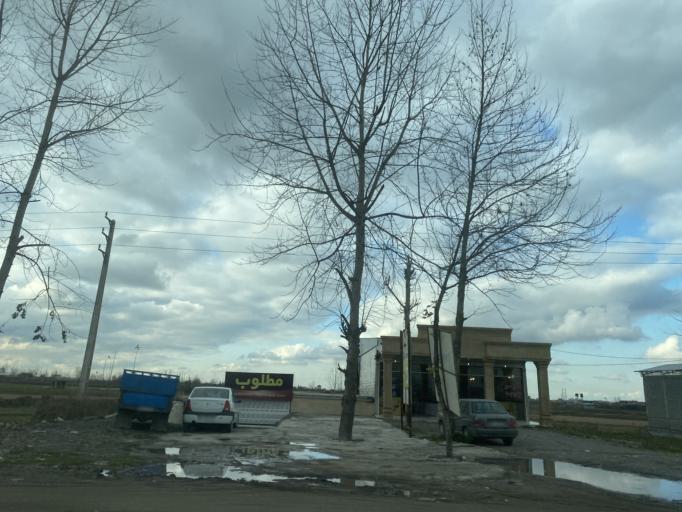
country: IR
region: Mazandaran
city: Amol
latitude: 36.4414
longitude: 52.3811
